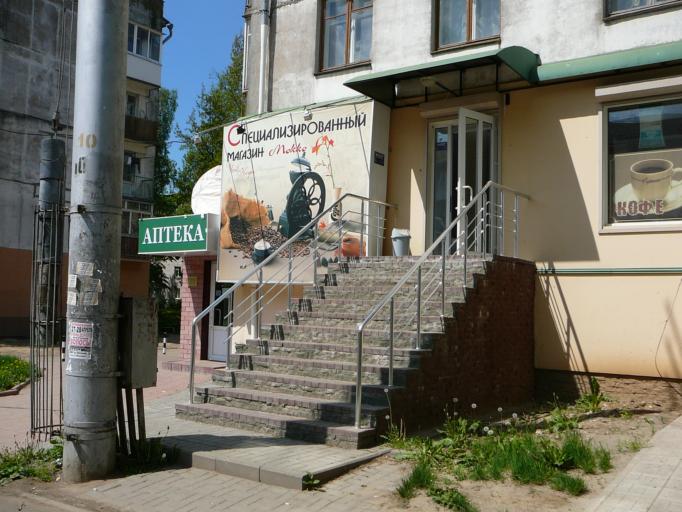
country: RU
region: Smolensk
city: Smolensk
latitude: 54.7701
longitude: 32.0221
